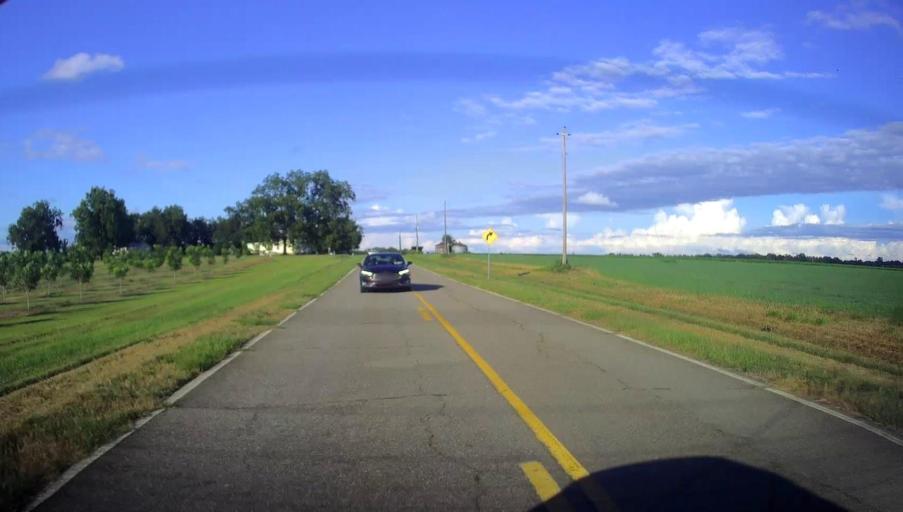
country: US
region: Georgia
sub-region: Bleckley County
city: Cochran
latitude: 32.3973
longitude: -83.4370
